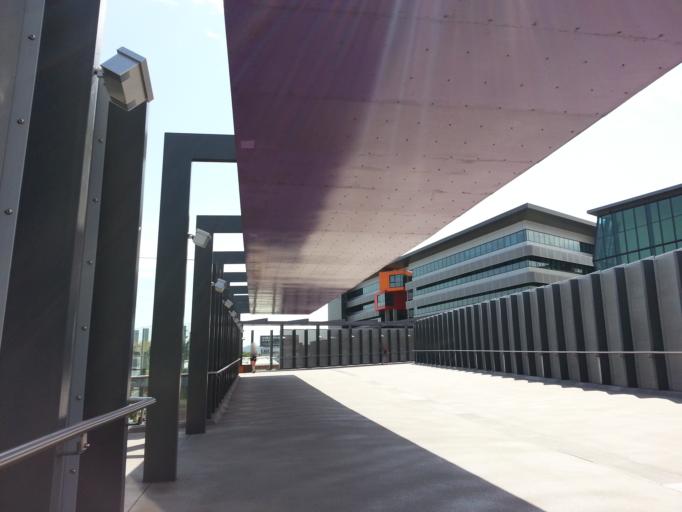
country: AU
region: Queensland
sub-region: Brisbane
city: Spring Hill
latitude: -27.4659
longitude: 153.0147
